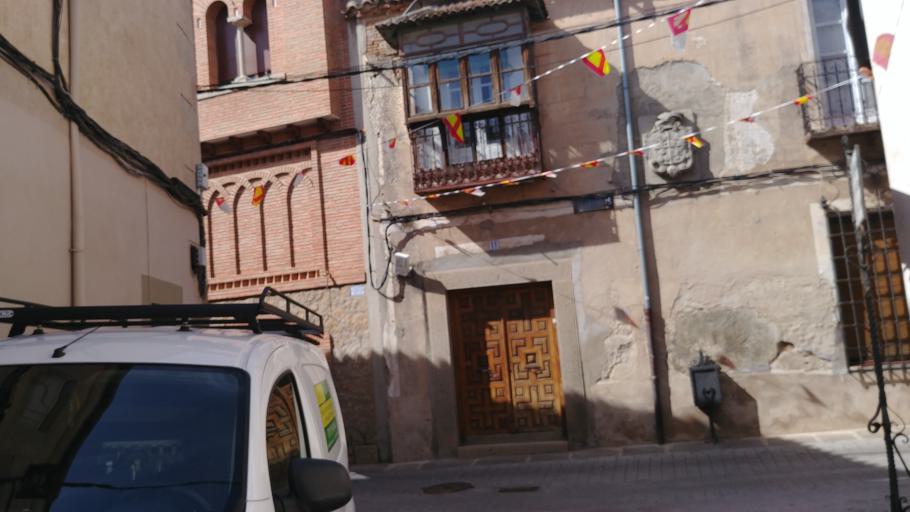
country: ES
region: Castille-La Mancha
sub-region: Province of Toledo
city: Oropesa
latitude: 39.9182
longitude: -5.1744
